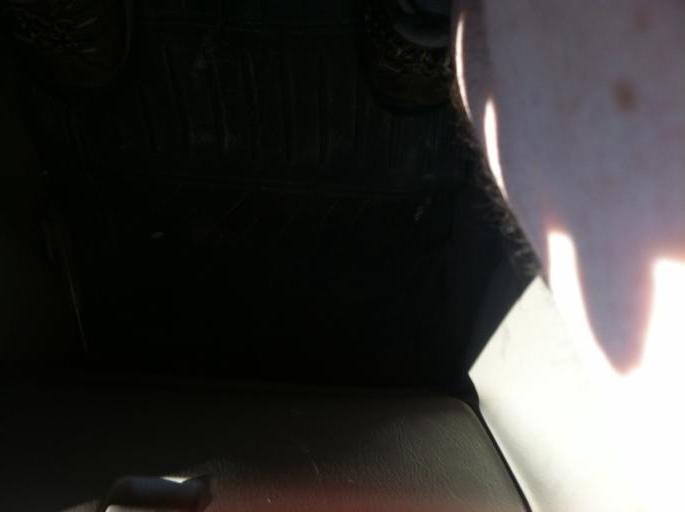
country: US
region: Massachusetts
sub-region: Suffolk County
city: Winthrop
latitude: 42.3831
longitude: -70.9729
